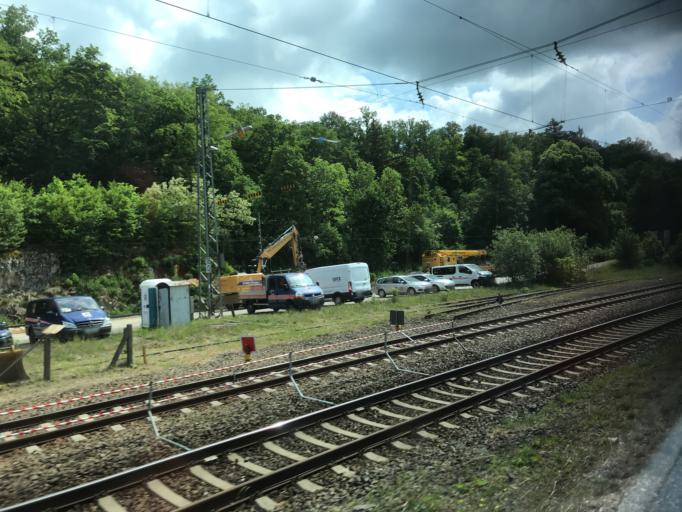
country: DE
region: Baden-Wuerttemberg
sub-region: Tuebingen Region
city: Westerstetten
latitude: 48.5249
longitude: 9.9438
